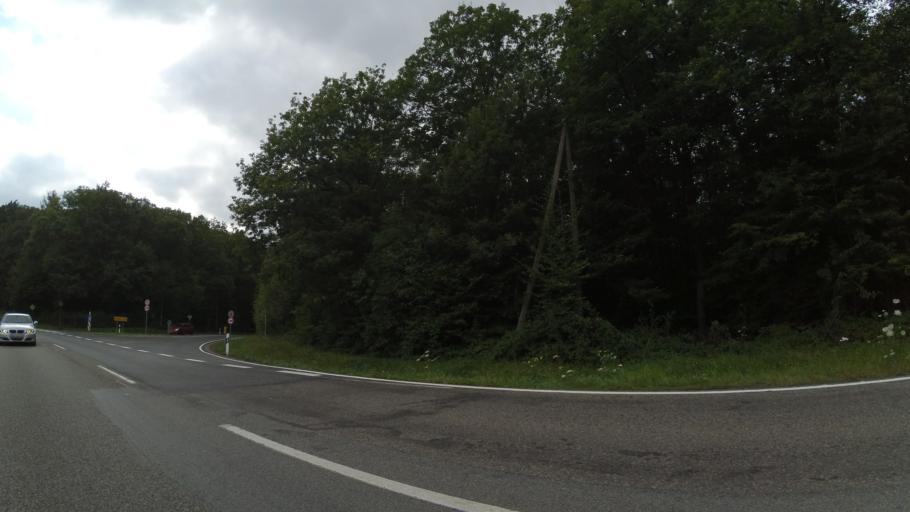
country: DE
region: Saarland
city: Riegelsberg
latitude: 49.2758
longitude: 6.9307
